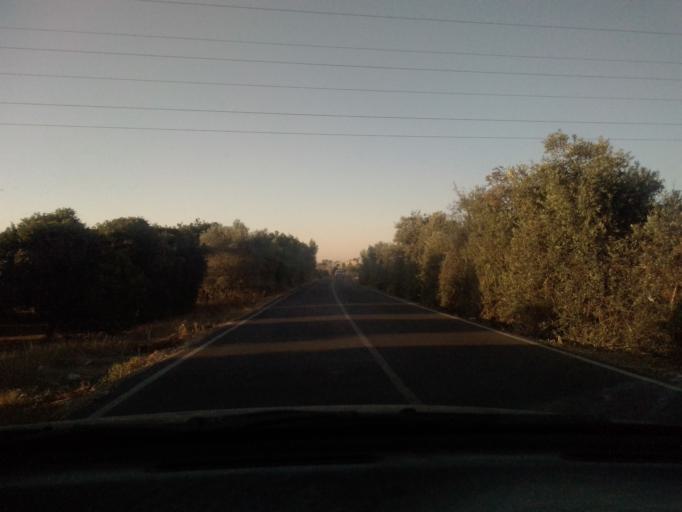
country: CY
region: Limassol
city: Ypsonas
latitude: 34.6655
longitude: 32.9621
